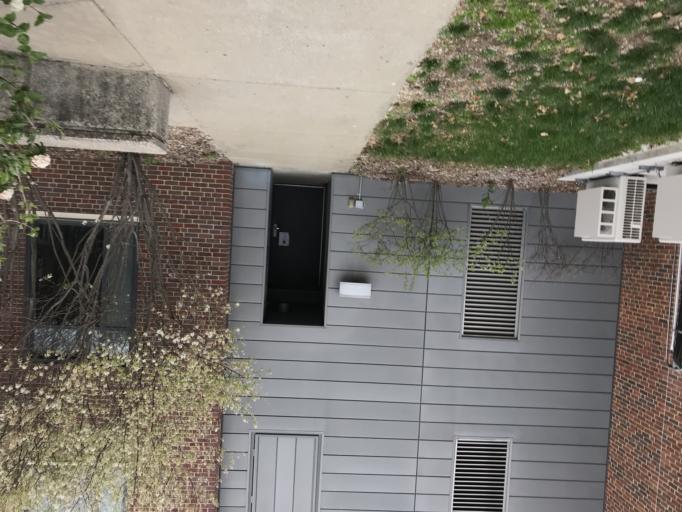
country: US
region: Kentucky
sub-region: Jefferson County
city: Audubon Park
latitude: 38.2127
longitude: -85.7605
